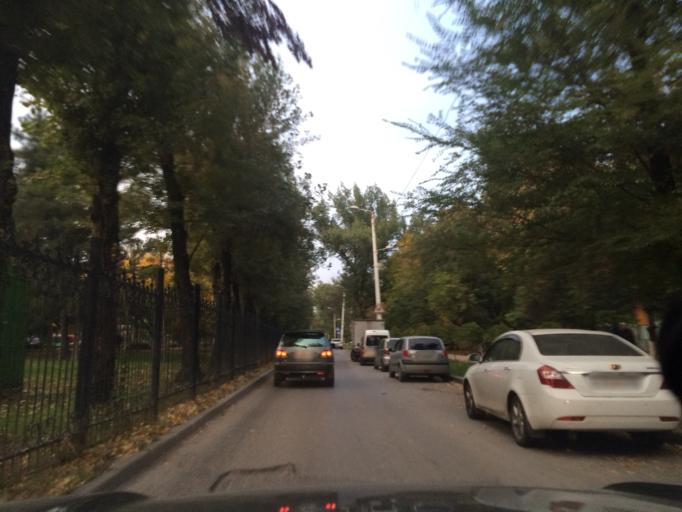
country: RU
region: Rostov
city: Rostov-na-Donu
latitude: 47.2043
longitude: 39.6341
